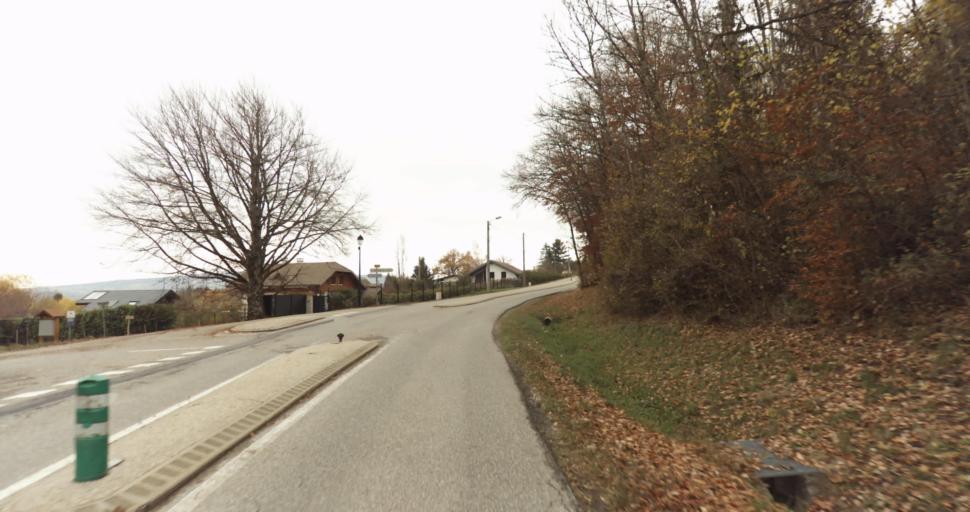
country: FR
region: Rhone-Alpes
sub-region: Departement de la Haute-Savoie
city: Saint-Martin-Bellevue
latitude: 45.9534
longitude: 6.1450
